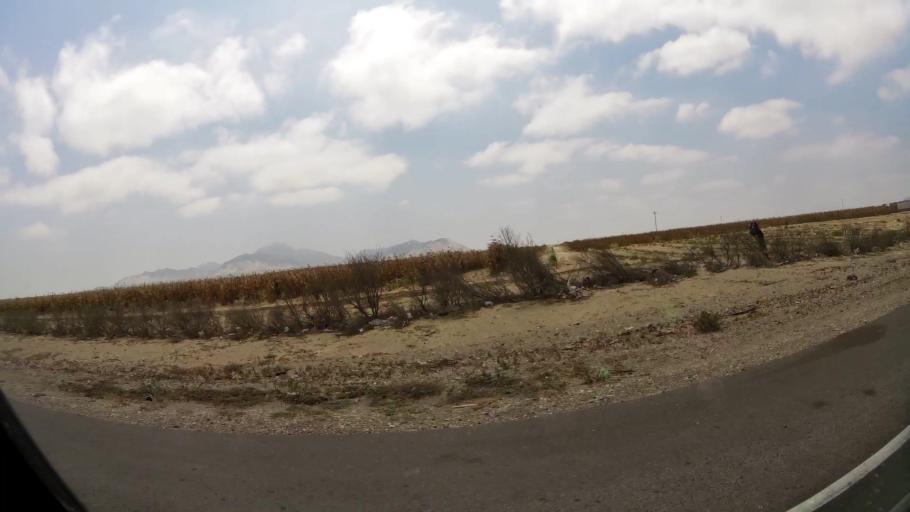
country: PE
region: La Libertad
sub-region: Ascope
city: Paijan
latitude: -7.6578
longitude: -79.3386
